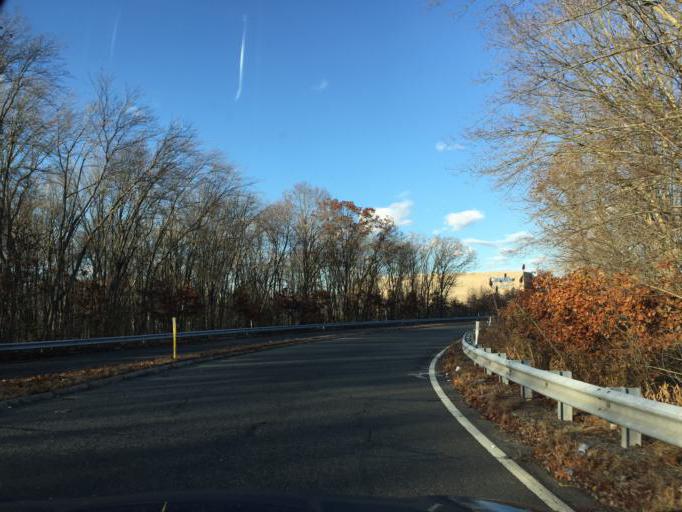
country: US
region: Massachusetts
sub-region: Bristol County
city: North Seekonk
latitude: 41.9029
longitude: -71.3582
